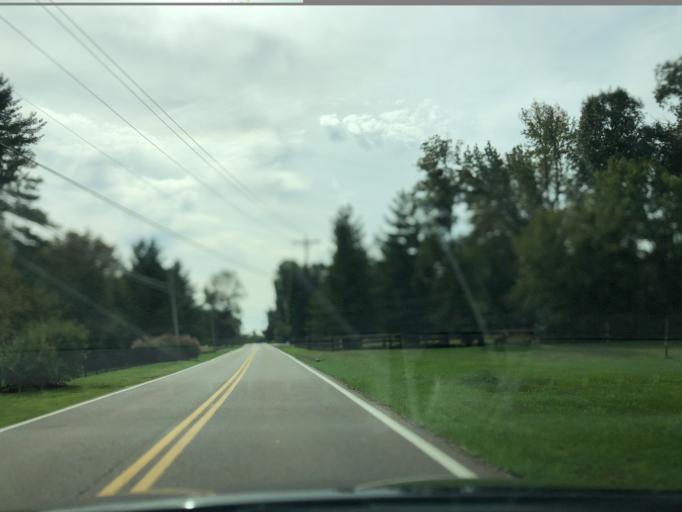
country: US
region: Ohio
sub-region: Hamilton County
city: The Village of Indian Hill
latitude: 39.2241
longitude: -84.3018
